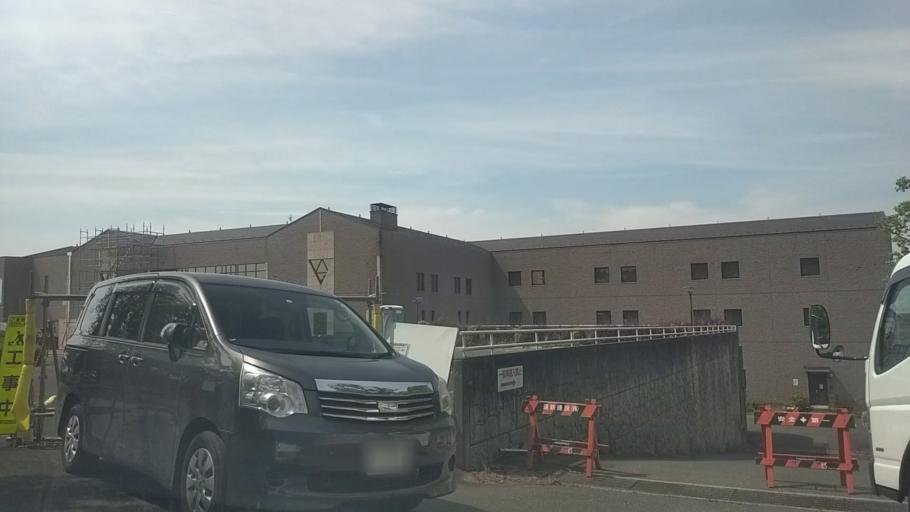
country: JP
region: Shizuoka
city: Kosai-shi
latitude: 34.7704
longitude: 137.6200
